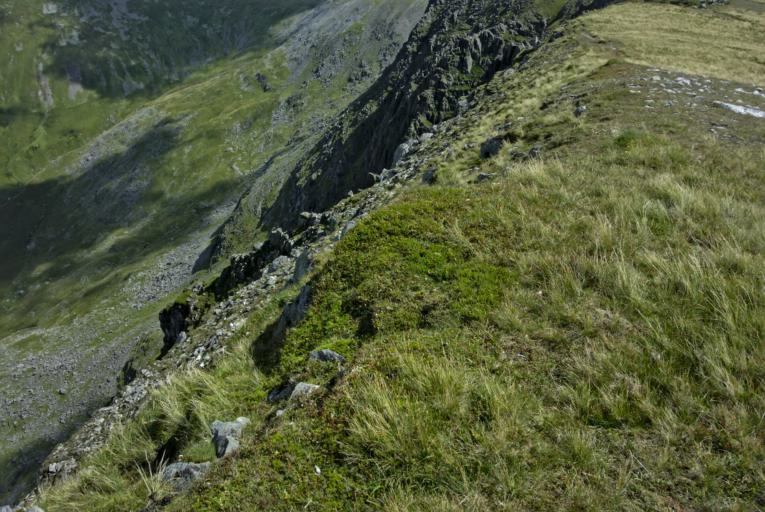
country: GB
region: Wales
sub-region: Gwynedd
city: Aber
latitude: 53.1477
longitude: -3.9914
